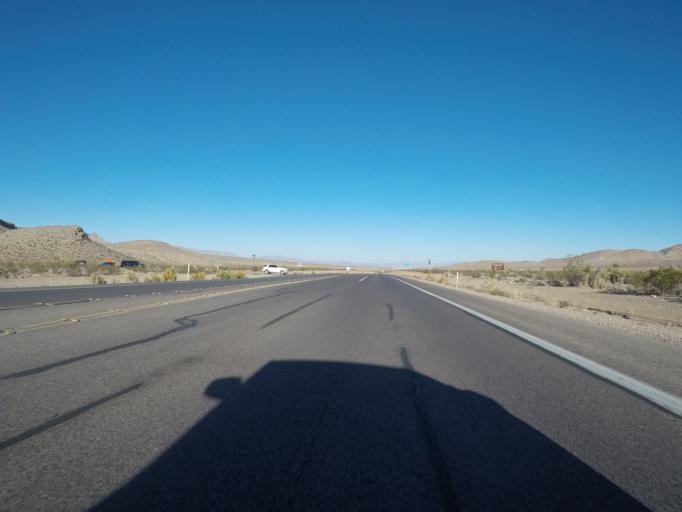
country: US
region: Nevada
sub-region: Clark County
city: Summerlin South
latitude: 36.1412
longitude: -115.4002
